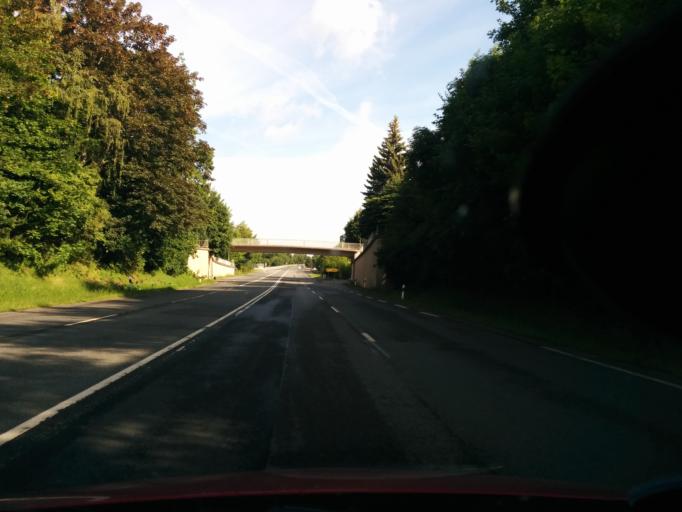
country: DE
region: Lower Saxony
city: Bad Harzburg
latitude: 51.8835
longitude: 10.5636
